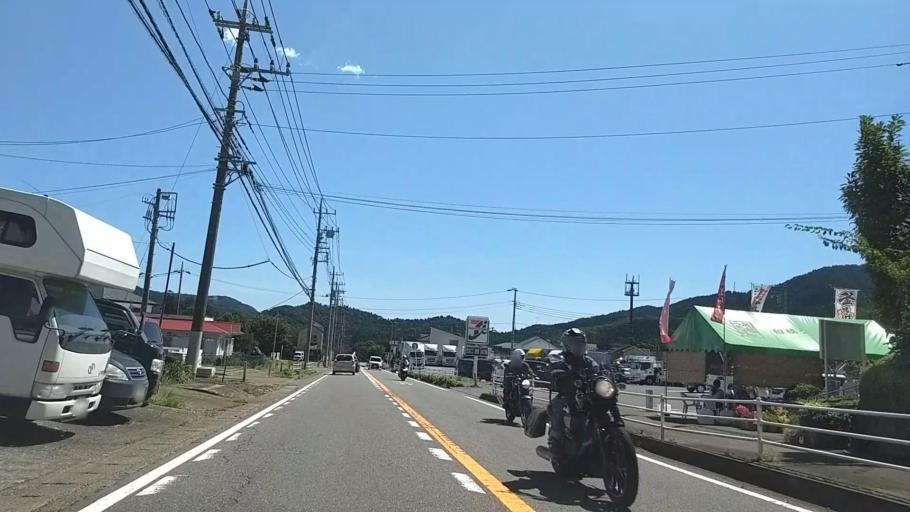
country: JP
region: Tokyo
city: Hachioji
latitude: 35.5691
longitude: 139.2411
